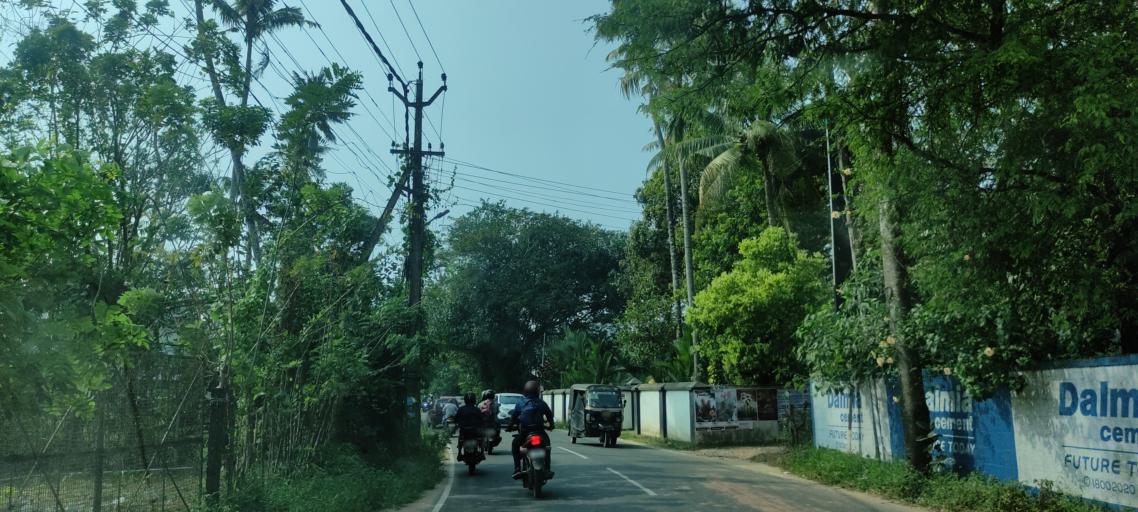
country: IN
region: Kerala
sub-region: Alappuzha
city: Vayalar
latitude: 9.6944
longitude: 76.3300
